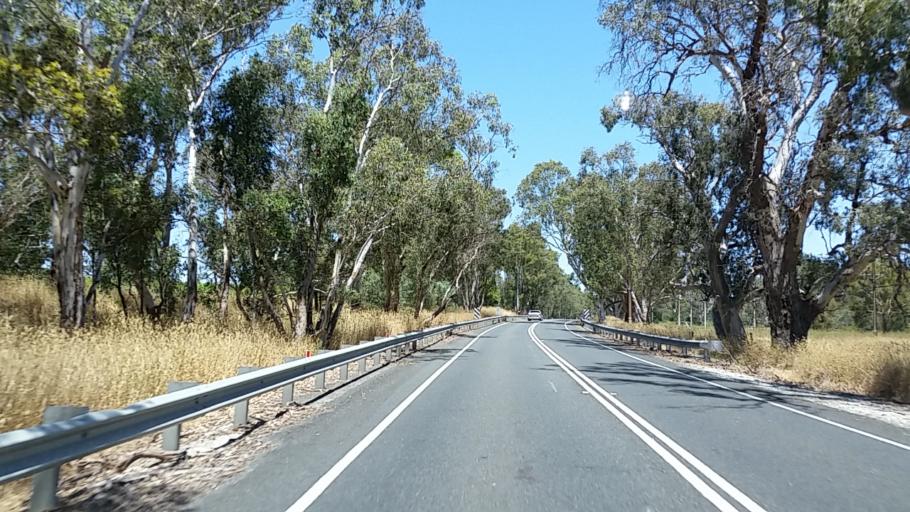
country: AU
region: South Australia
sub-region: Adelaide Hills
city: Birdwood
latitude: -34.8111
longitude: 138.9779
